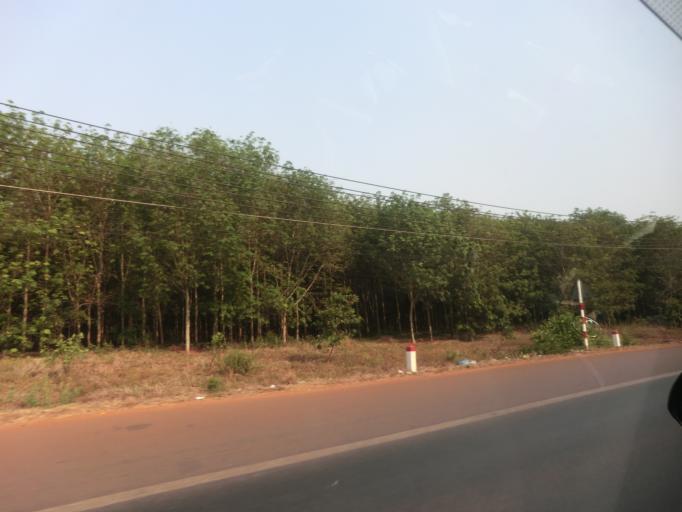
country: VN
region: Dong Nai
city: Thong Nhat
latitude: 11.0734
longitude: 107.1666
